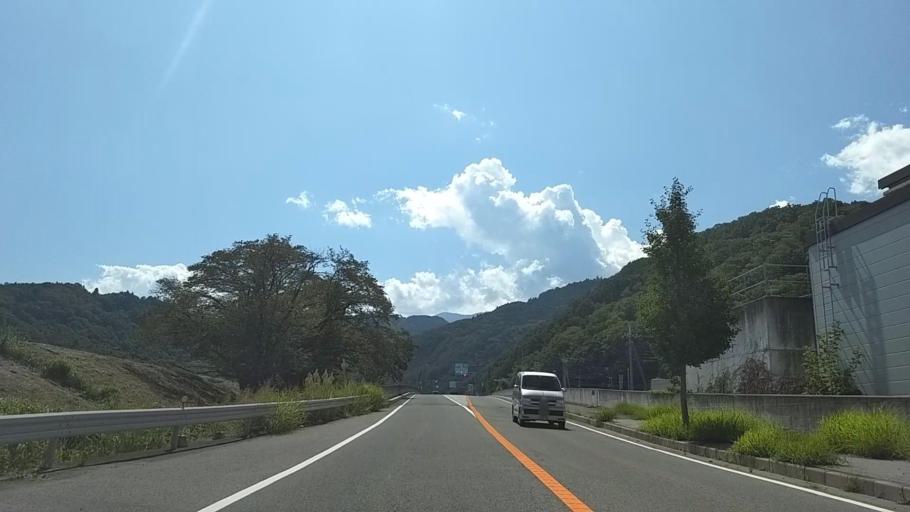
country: JP
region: Yamanashi
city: Ryuo
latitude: 35.5424
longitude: 138.4598
